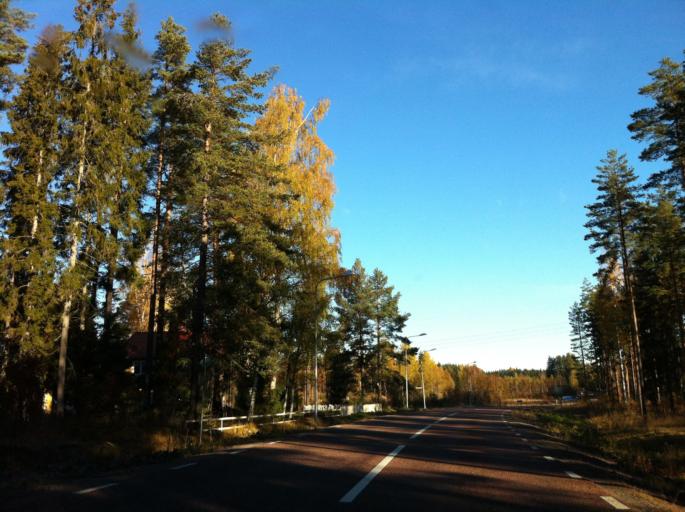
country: SE
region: Gaevleborg
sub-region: Gavle Kommun
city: Gavle
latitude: 60.5580
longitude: 17.1224
